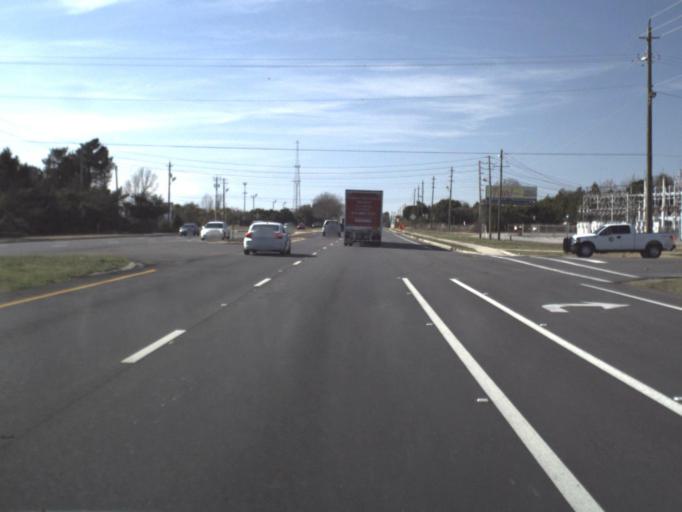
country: US
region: Florida
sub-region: Bay County
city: Laguna Beach
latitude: 30.2267
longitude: -85.8768
